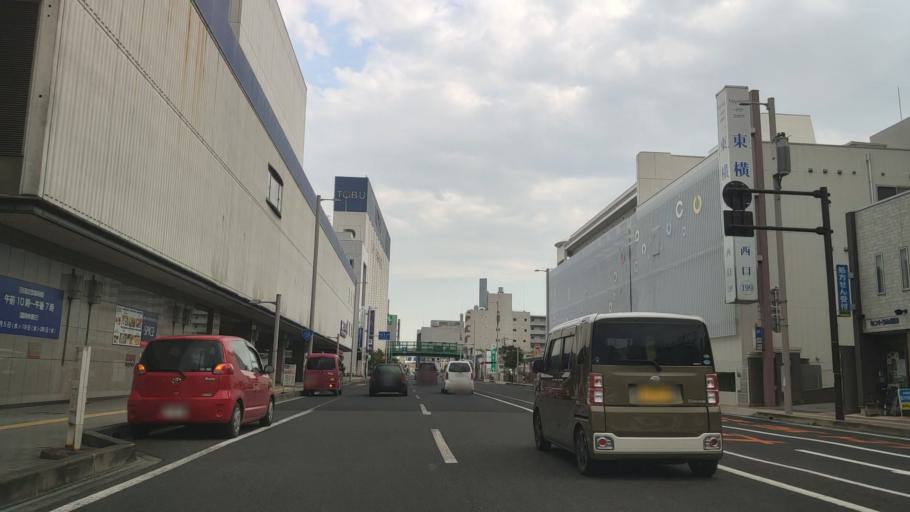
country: JP
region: Tochigi
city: Utsunomiya-shi
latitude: 36.5602
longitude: 139.8798
